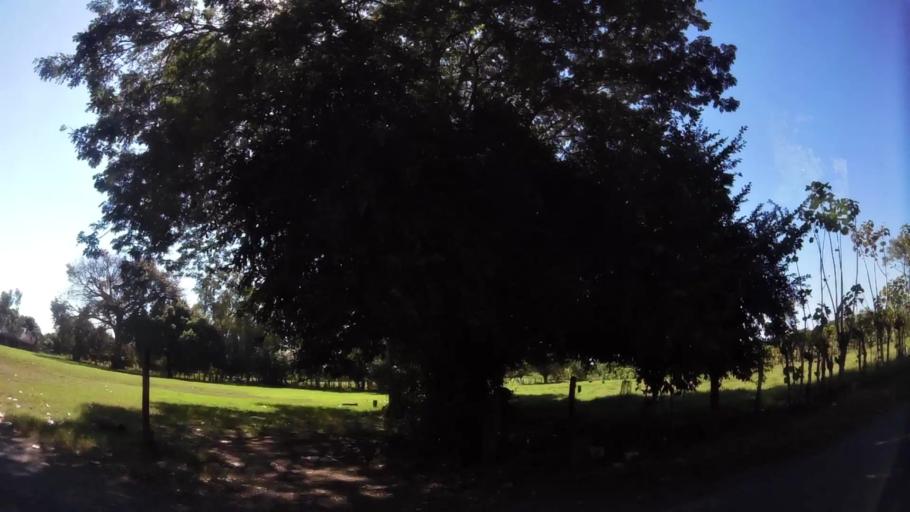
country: GT
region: Escuintla
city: Iztapa
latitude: 13.9247
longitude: -90.5859
